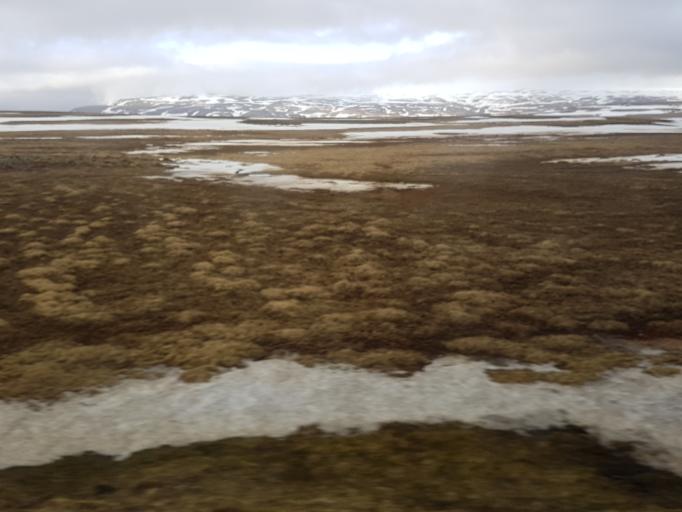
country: IS
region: South
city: Hveragerdi
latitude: 64.2096
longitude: -21.3105
